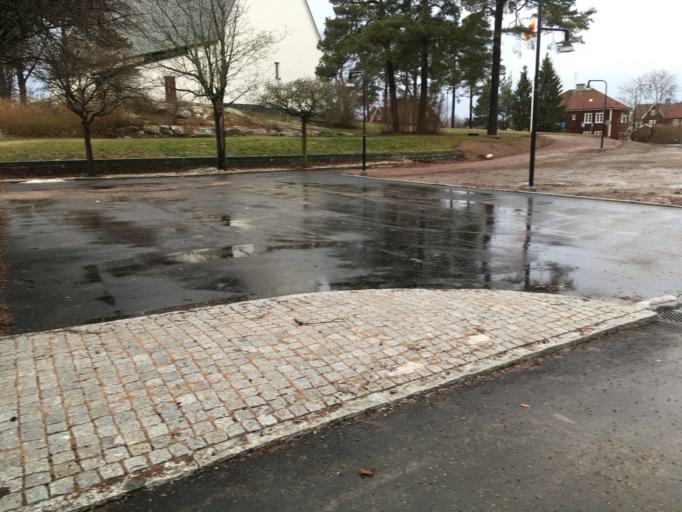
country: SE
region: Vaermland
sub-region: Hammaro Kommun
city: Skoghall
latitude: 59.3226
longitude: 13.4650
